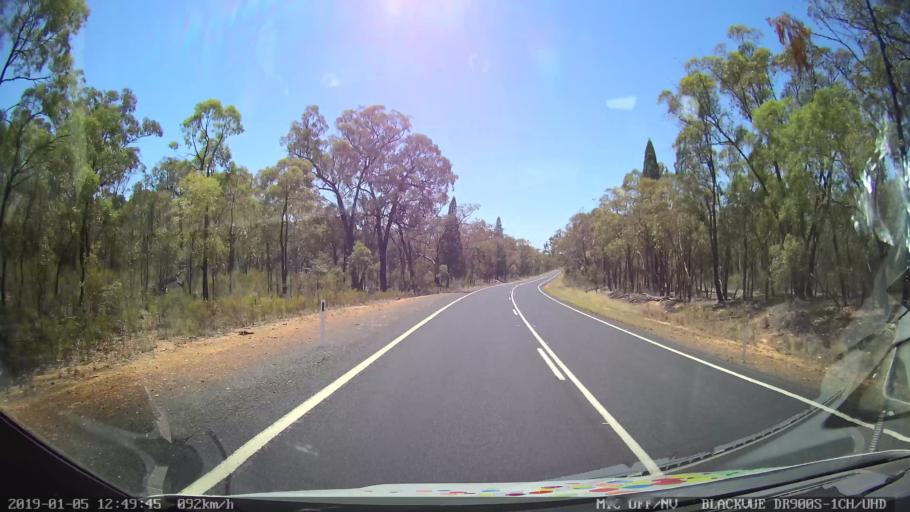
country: AU
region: New South Wales
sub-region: Warrumbungle Shire
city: Coonabarabran
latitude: -31.1176
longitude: 149.6121
